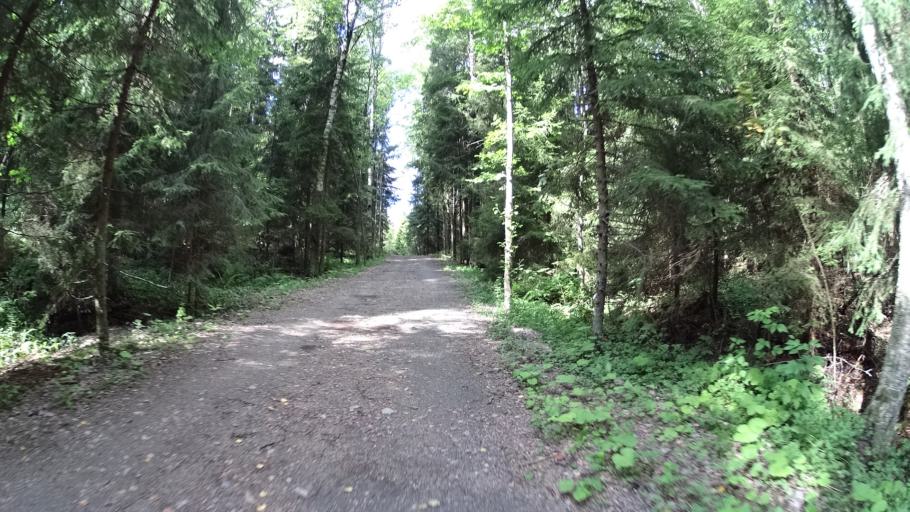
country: FI
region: Uusimaa
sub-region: Helsinki
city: Espoo
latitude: 60.2333
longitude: 24.6256
